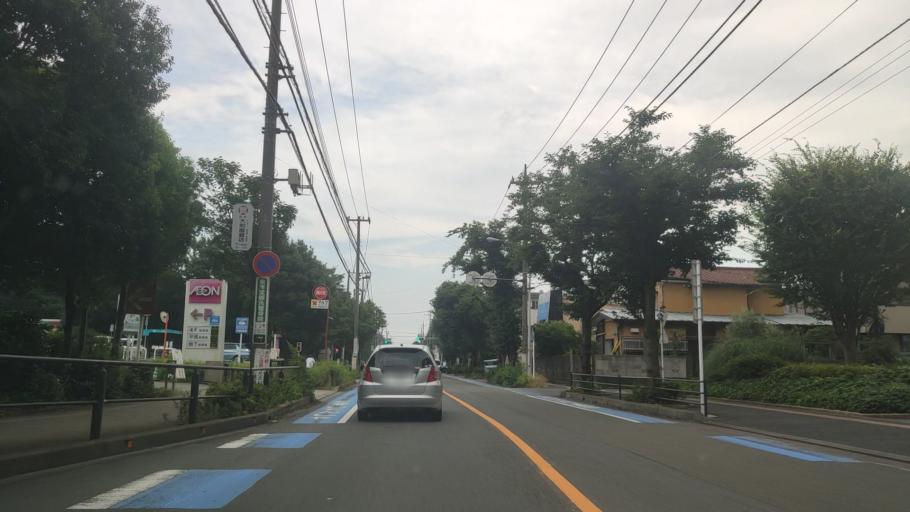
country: JP
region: Kanagawa
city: Minami-rinkan
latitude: 35.4888
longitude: 139.4564
